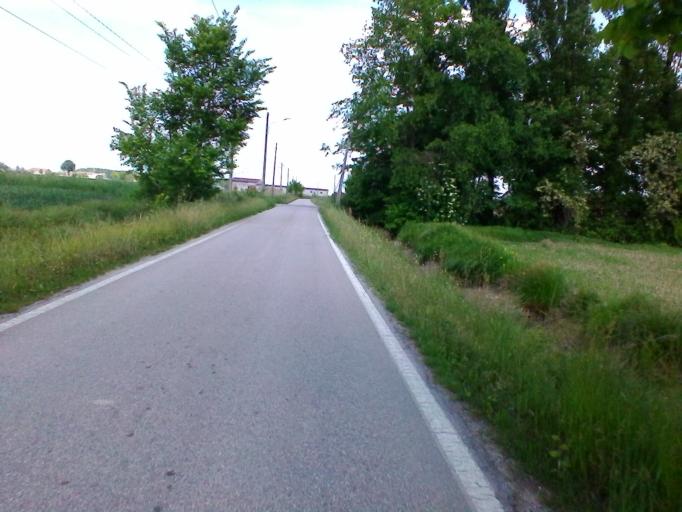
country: IT
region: Lombardy
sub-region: Provincia di Mantova
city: Sant'Antonio
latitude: 45.2256
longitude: 10.8196
